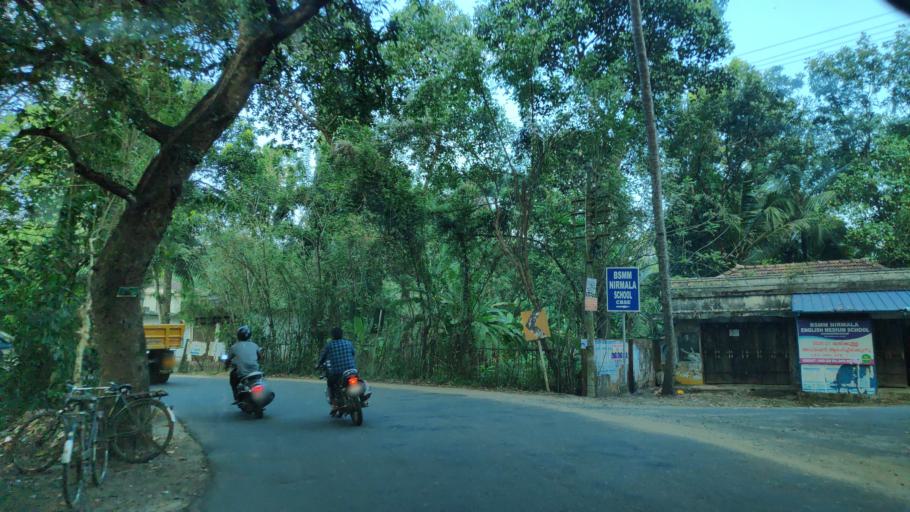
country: IN
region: Kerala
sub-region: Alappuzha
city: Shertallai
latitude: 9.6747
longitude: 76.3911
